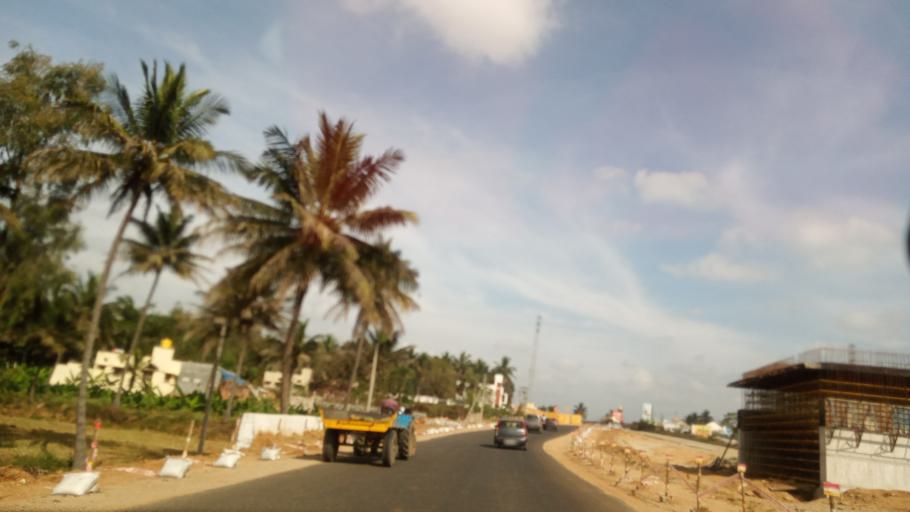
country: IN
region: Karnataka
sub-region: Mandya
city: Mandya
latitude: 12.4994
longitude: 76.8181
